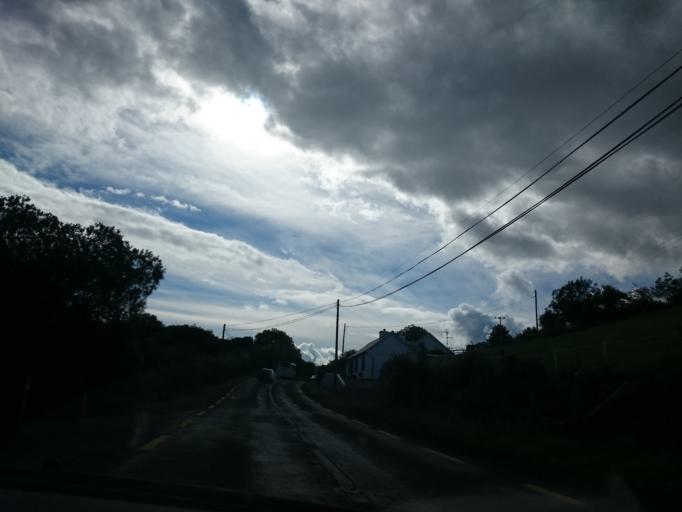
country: IE
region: Connaught
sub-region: Maigh Eo
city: Westport
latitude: 53.9029
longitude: -9.5821
